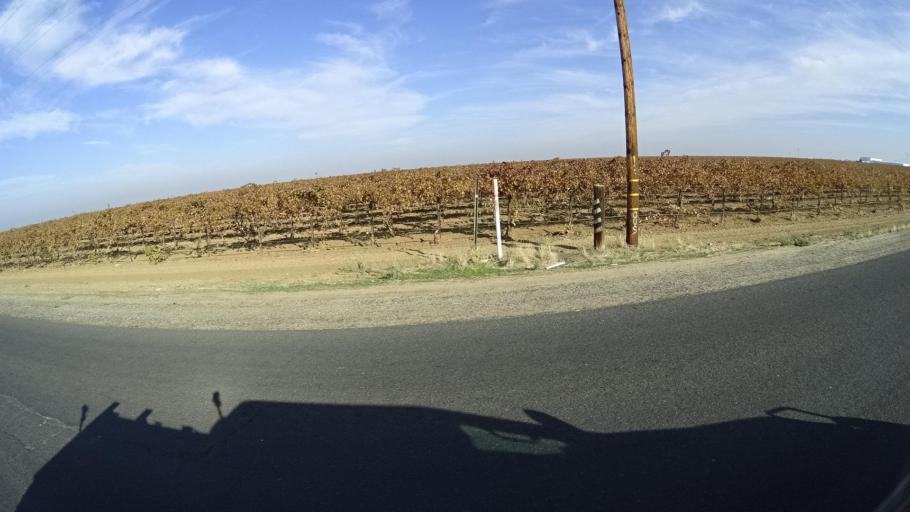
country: US
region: California
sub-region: Kern County
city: McFarland
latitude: 35.6021
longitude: -119.1565
